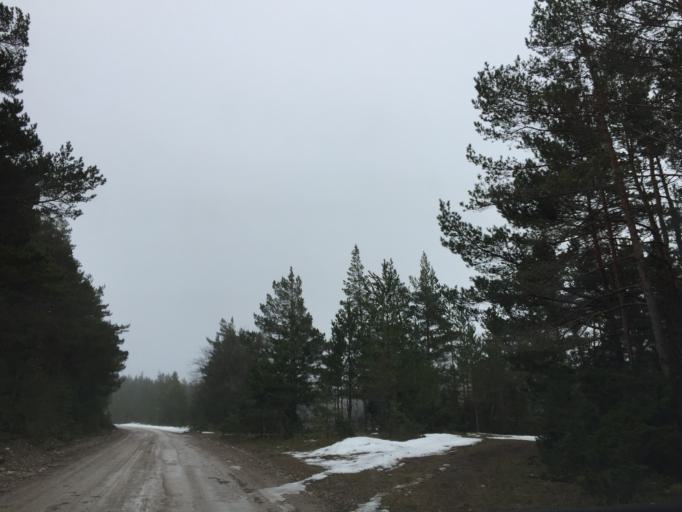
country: EE
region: Saare
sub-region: Kuressaare linn
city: Kuressaare
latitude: 58.5010
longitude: 21.9752
